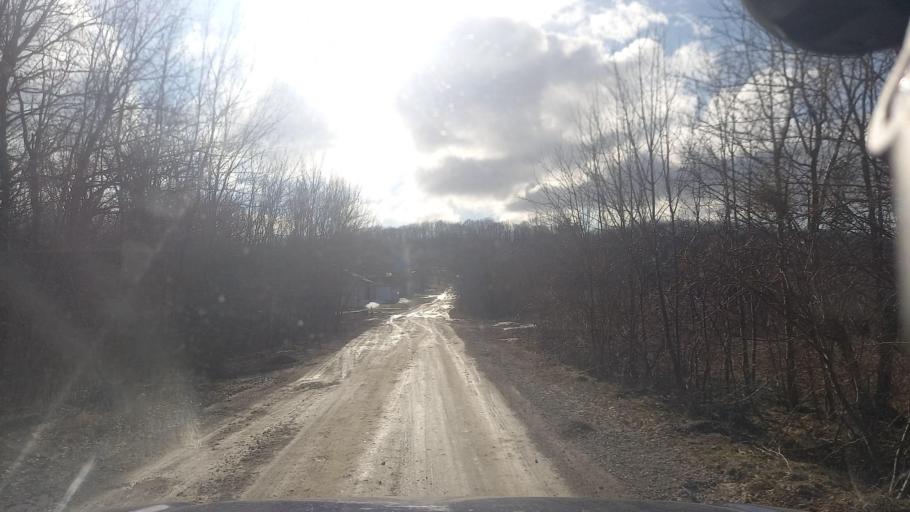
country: RU
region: Krasnodarskiy
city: Goryachiy Klyuch
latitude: 44.6894
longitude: 38.9832
